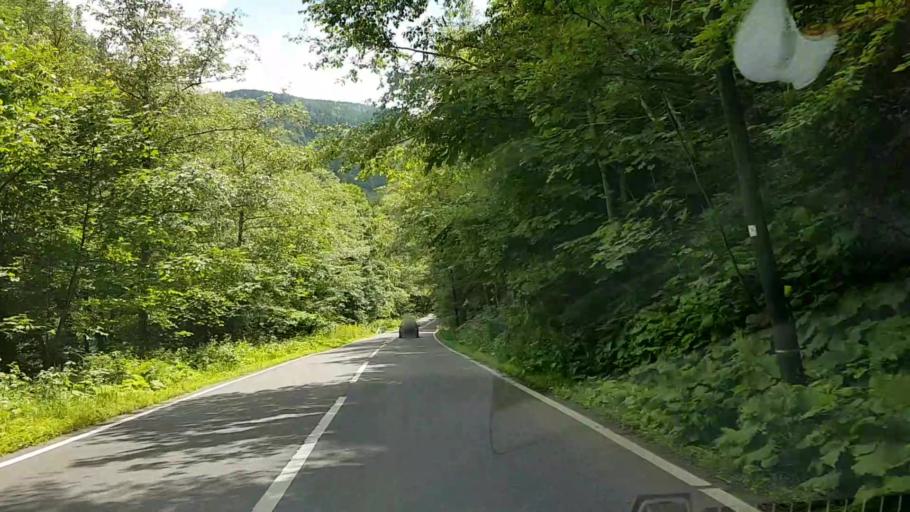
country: RO
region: Suceava
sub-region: Comuna Crucea
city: Crucea
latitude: 47.3077
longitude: 25.6233
